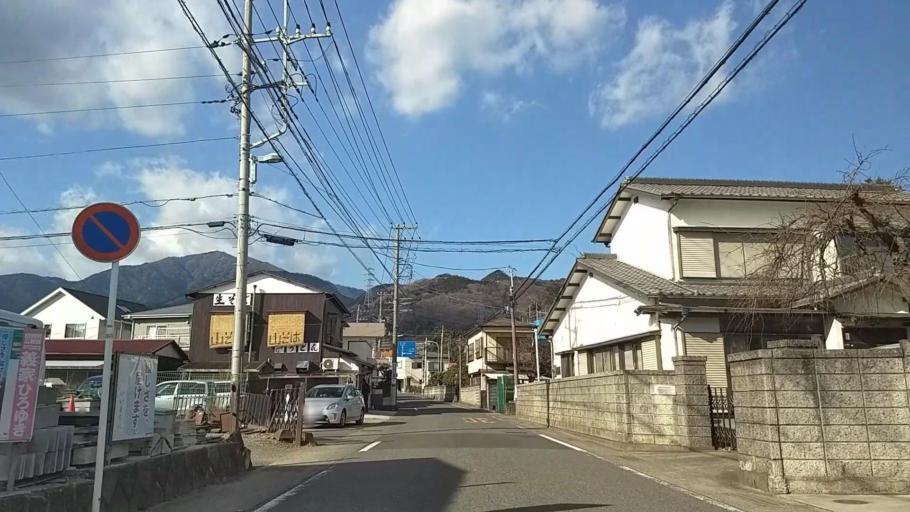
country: JP
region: Kanagawa
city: Isehara
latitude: 35.4130
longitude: 139.2852
